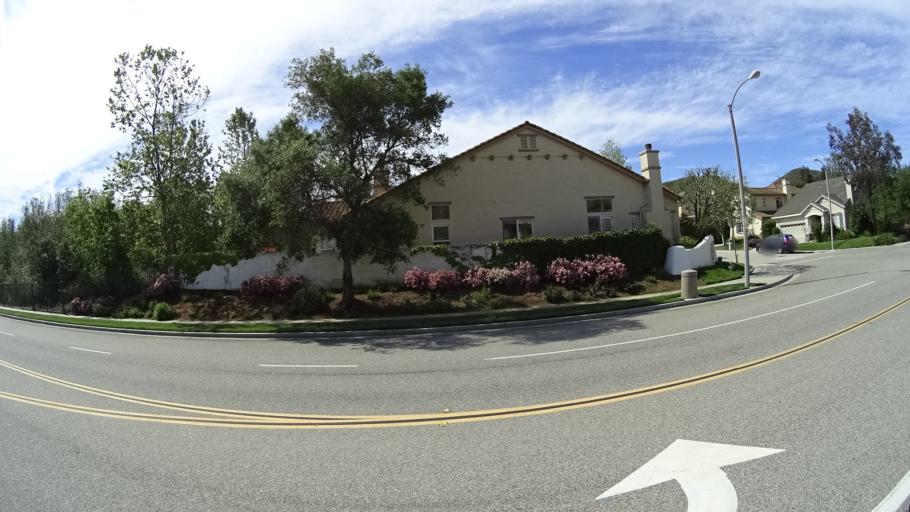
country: US
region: California
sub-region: Ventura County
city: Casa Conejo
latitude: 34.1730
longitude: -118.9739
